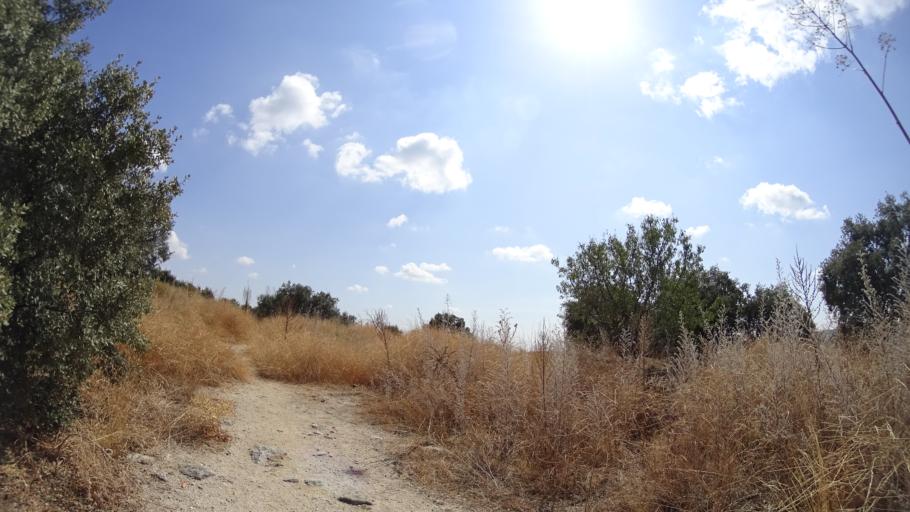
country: ES
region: Madrid
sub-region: Provincia de Madrid
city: Galapagar
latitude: 40.5821
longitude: -3.9881
